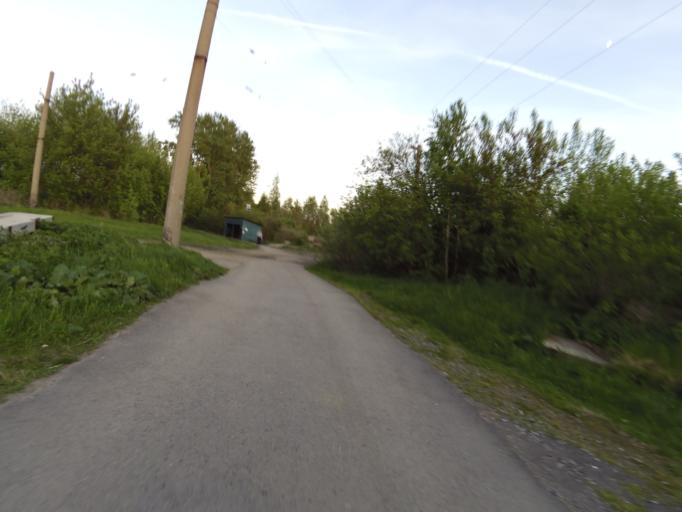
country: RU
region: Sverdlovsk
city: Shirokaya Rechka
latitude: 56.8444
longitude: 60.4990
